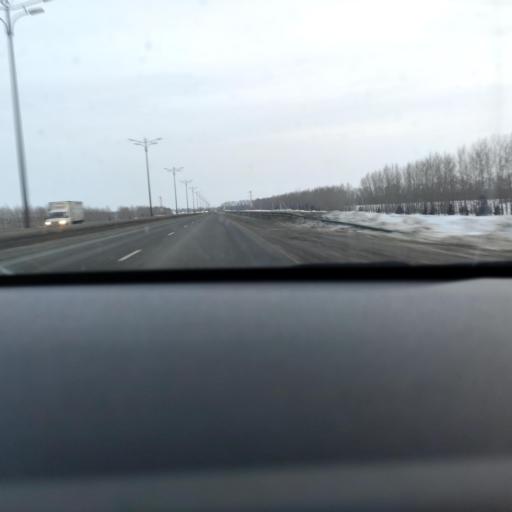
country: RU
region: Tatarstan
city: Stolbishchi
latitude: 55.6875
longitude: 49.2426
